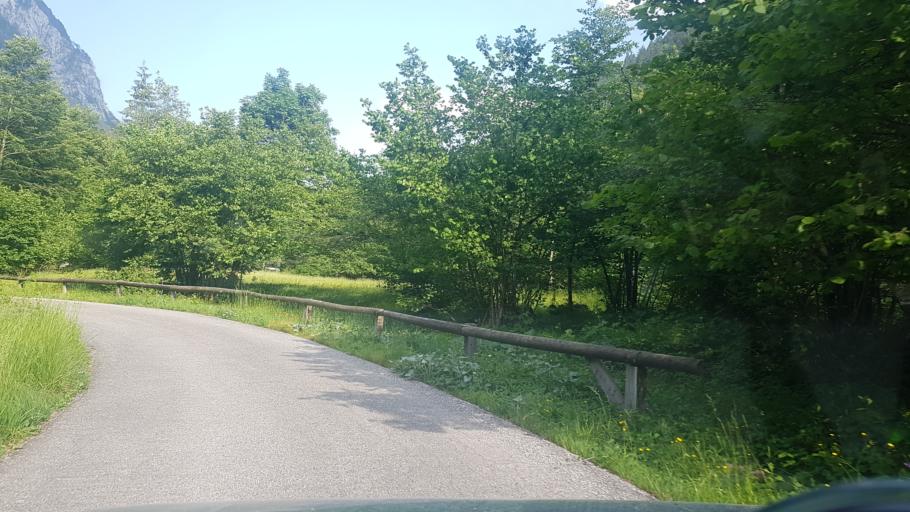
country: IT
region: Friuli Venezia Giulia
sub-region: Provincia di Udine
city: Pontebba
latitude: 46.5265
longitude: 13.2484
